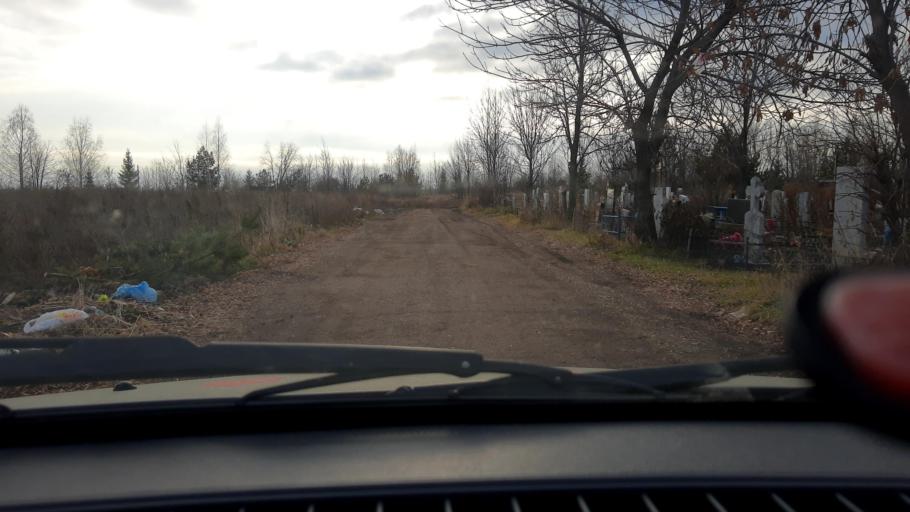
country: RU
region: Bashkortostan
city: Ufa
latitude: 54.8581
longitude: 56.1640
